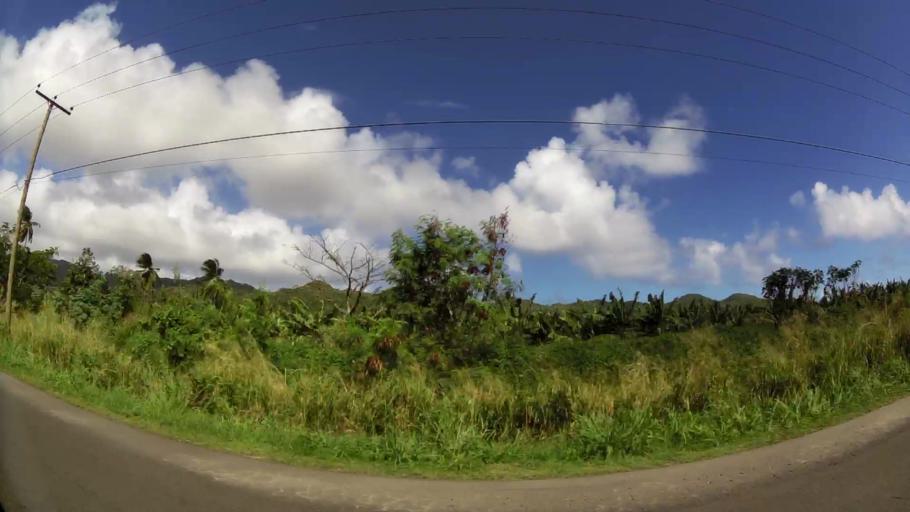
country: LC
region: Dennery Quarter
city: Dennery
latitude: 13.9284
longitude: -60.9000
